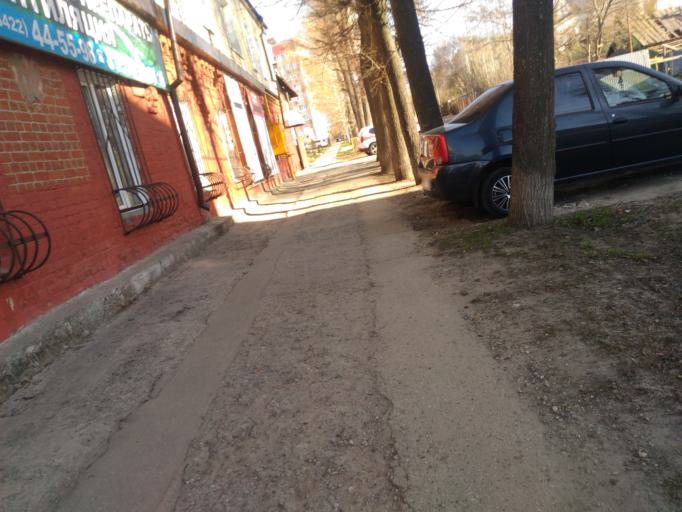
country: RU
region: Ulyanovsk
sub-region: Ulyanovskiy Rayon
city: Ulyanovsk
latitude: 54.3304
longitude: 48.3954
